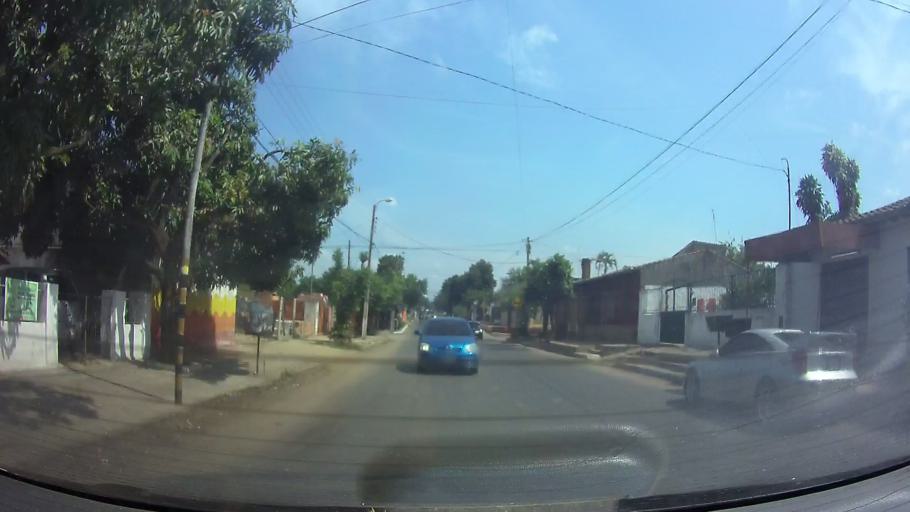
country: PY
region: Central
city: San Lorenzo
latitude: -25.3459
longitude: -57.4929
